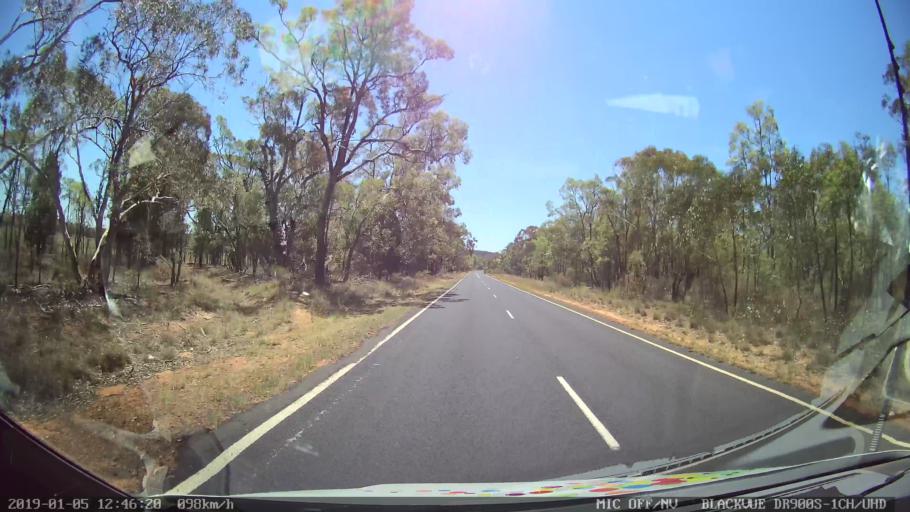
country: AU
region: New South Wales
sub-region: Warrumbungle Shire
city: Coonabarabran
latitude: -31.1190
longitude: 149.5613
